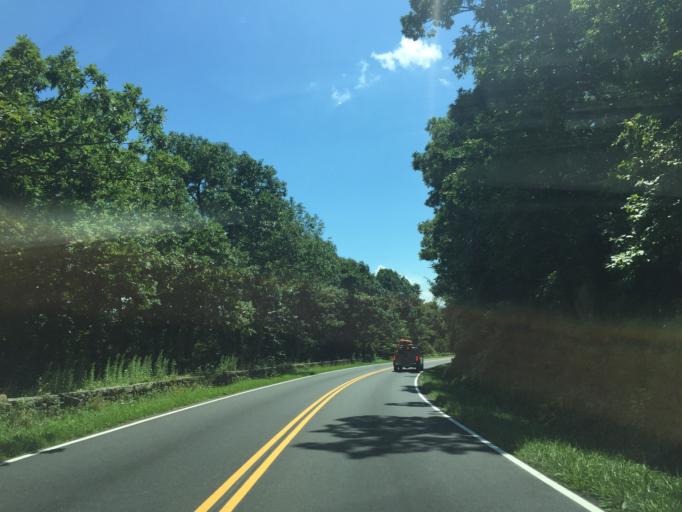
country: US
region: Virginia
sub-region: Rappahannock County
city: Washington
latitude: 38.7569
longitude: -78.2841
